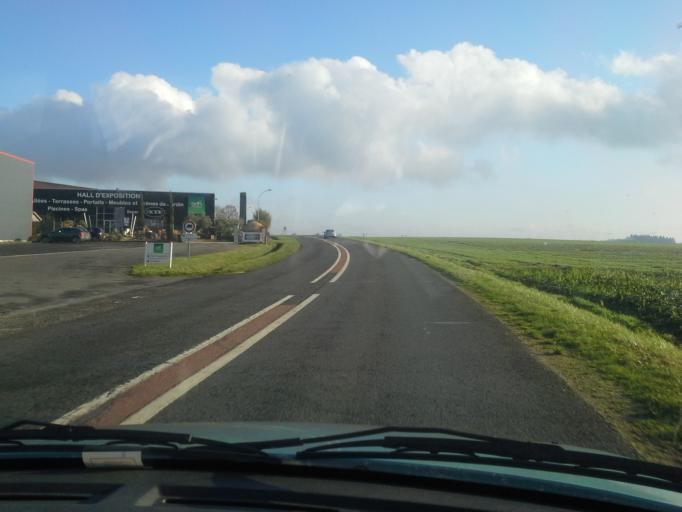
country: FR
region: Centre
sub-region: Departement du Loir-et-Cher
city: Villiers-sur-Loir
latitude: 47.7994
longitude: 1.0003
